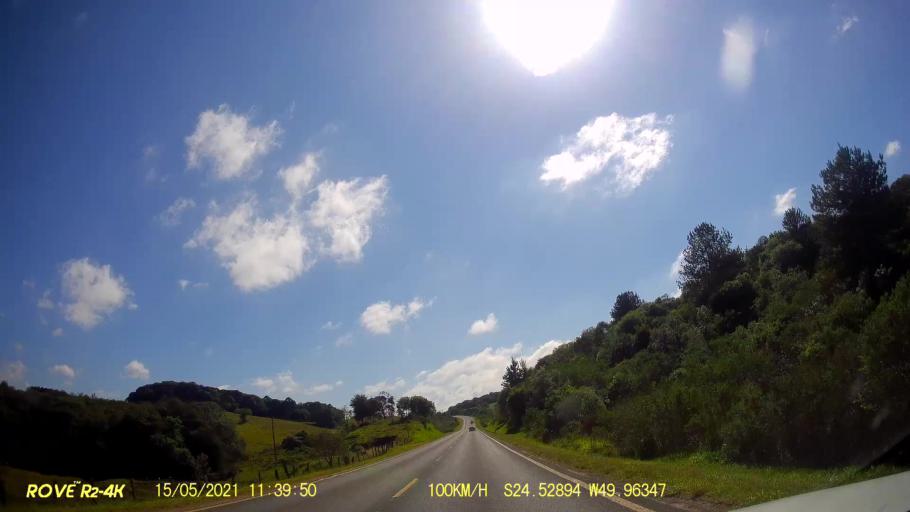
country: BR
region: Parana
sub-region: Pirai Do Sul
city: Pirai do Sul
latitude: -24.5292
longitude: -49.9634
